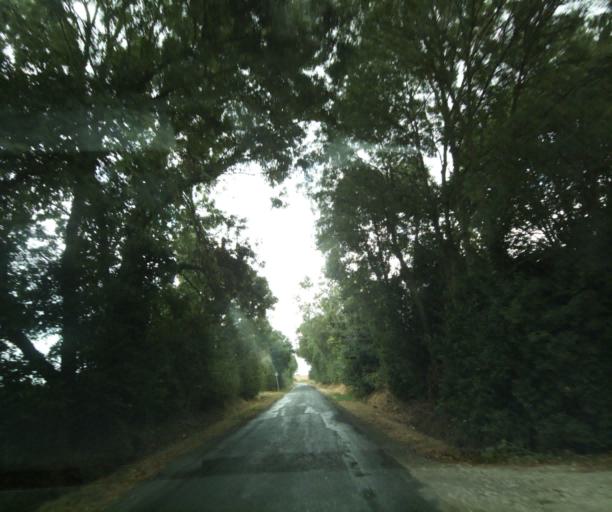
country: FR
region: Poitou-Charentes
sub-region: Departement de la Charente-Maritime
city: Tonnay-Charente
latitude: 45.9423
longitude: -0.8730
